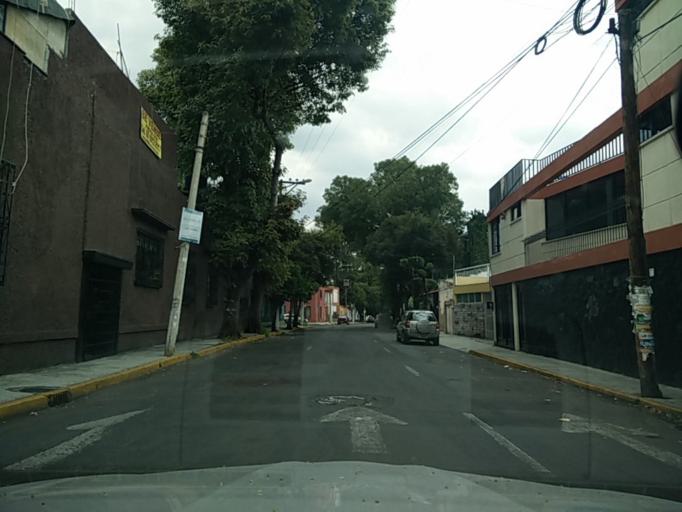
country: MX
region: Mexico City
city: Coyoacan
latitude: 19.3525
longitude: -99.1568
